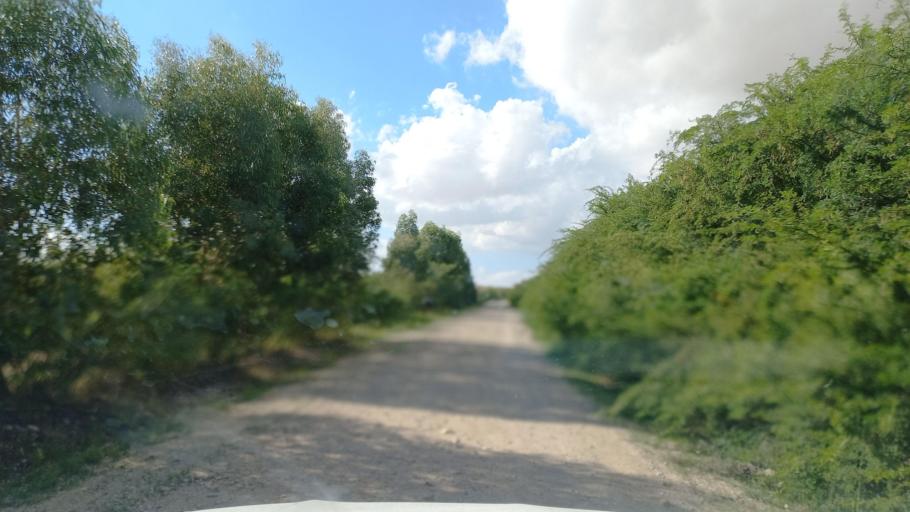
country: TN
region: Al Qasrayn
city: Sbiba
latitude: 35.3361
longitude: 9.0812
